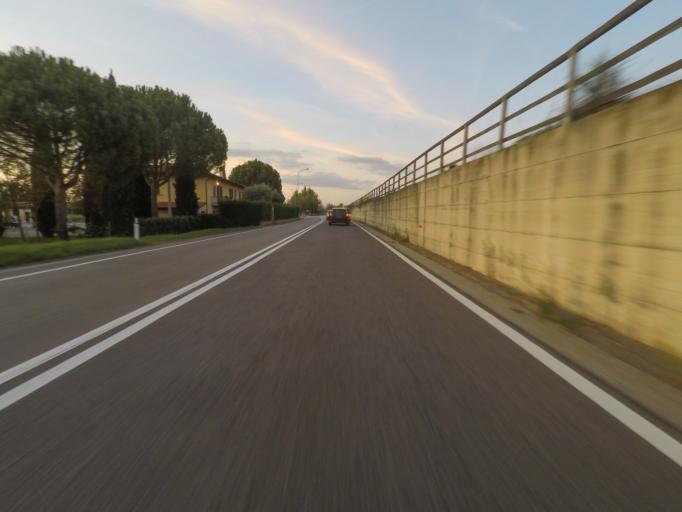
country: IT
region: Tuscany
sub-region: Provincia di Siena
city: Sinalunga
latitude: 43.2098
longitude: 11.7620
